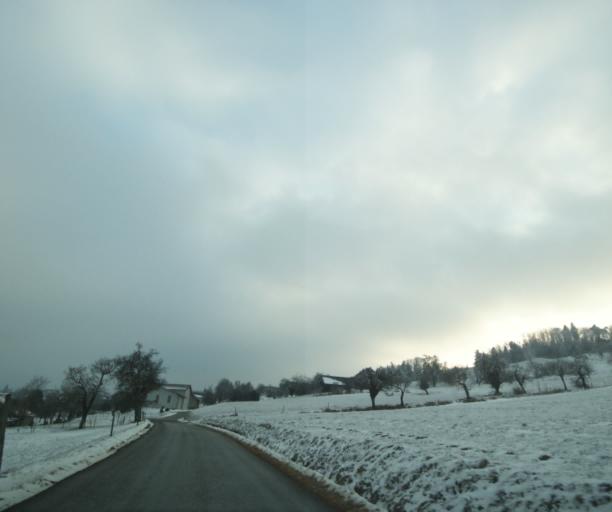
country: FR
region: Rhone-Alpes
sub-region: Departement de la Haute-Savoie
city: Reignier-Esery
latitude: 46.1338
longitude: 6.2371
